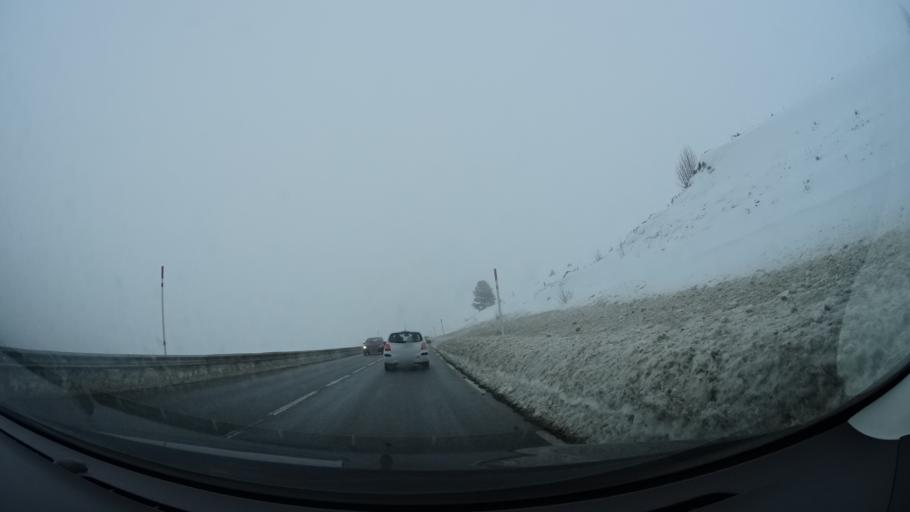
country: AD
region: Encamp
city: Pas de la Casa
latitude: 42.5590
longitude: 1.7711
